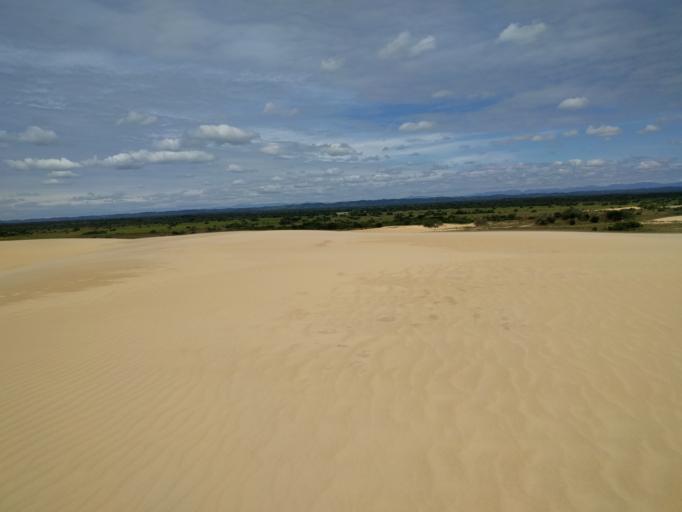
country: BO
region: Santa Cruz
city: Santa Cruz de la Sierra
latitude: -17.9412
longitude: -63.1597
